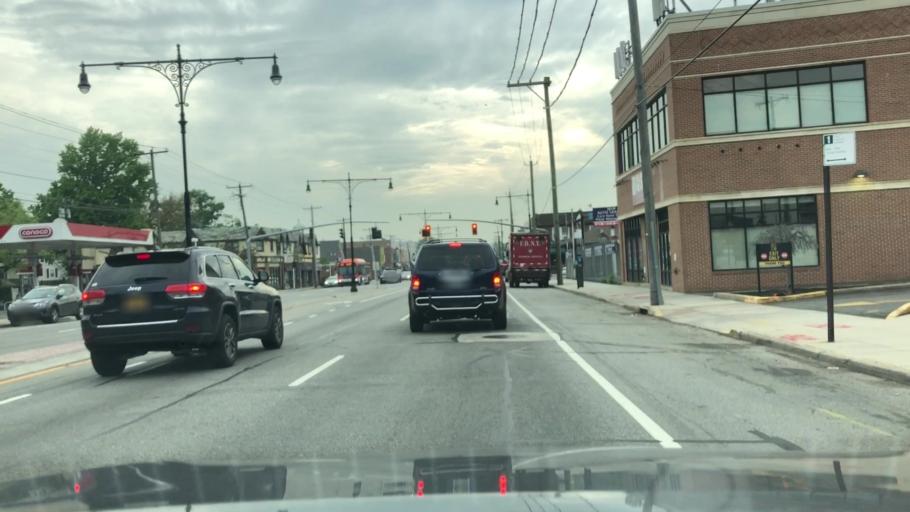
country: US
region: New York
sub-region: Nassau County
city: Bellerose
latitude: 40.7258
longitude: -73.7195
